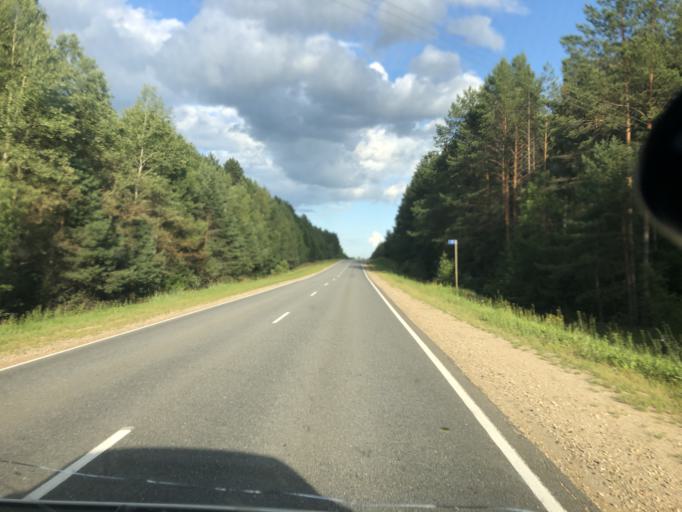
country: RU
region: Kaluga
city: Yukhnov
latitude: 54.7106
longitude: 35.2524
